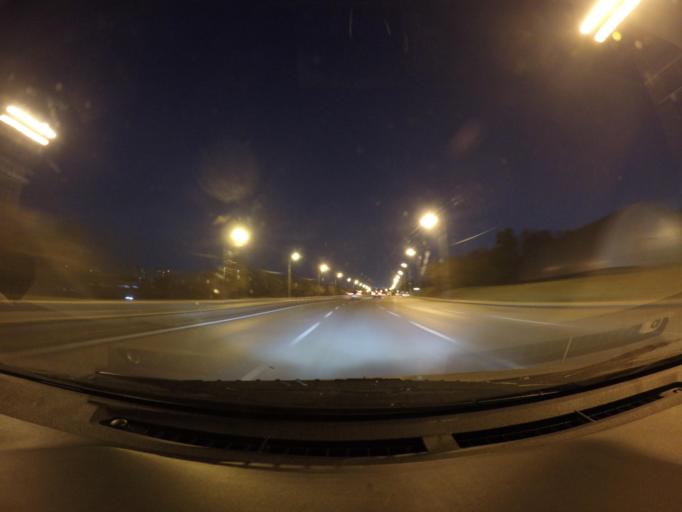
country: RU
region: Moscow
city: Sokol'niki
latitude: 55.8137
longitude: 37.6875
